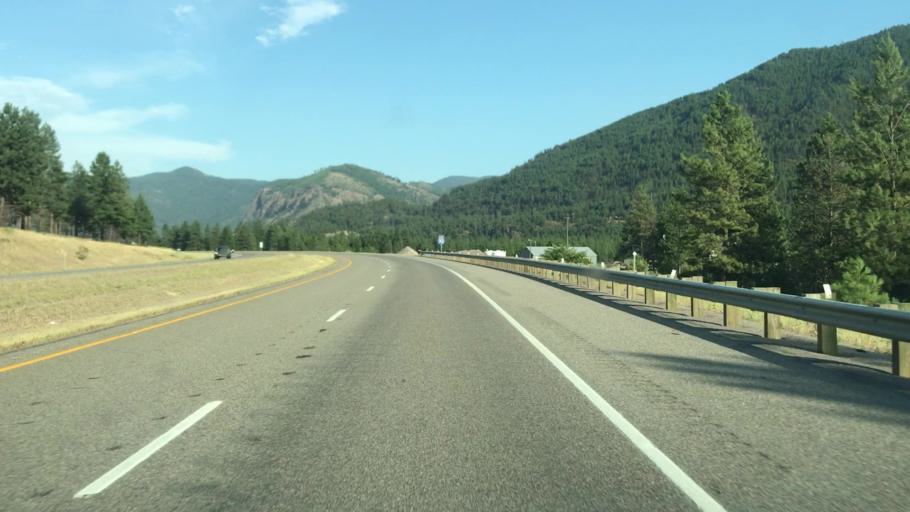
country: US
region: Montana
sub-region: Missoula County
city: Frenchtown
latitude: 47.0025
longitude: -114.4880
